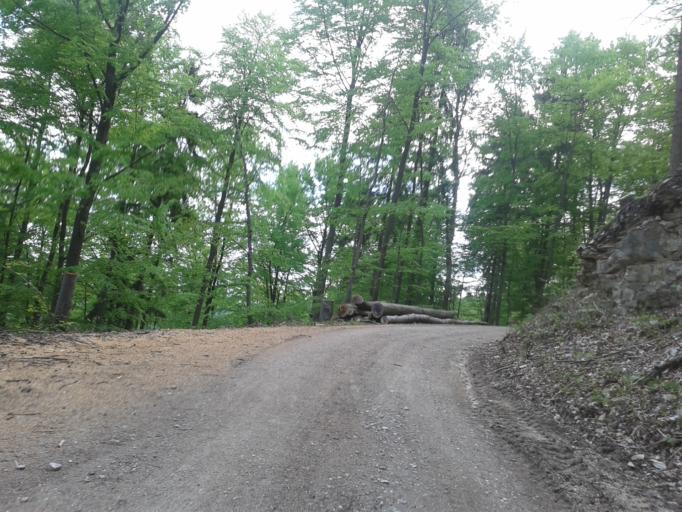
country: DE
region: Baden-Wuerttemberg
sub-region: Tuebingen Region
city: Blaubeuren
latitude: 48.3982
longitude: 9.7883
